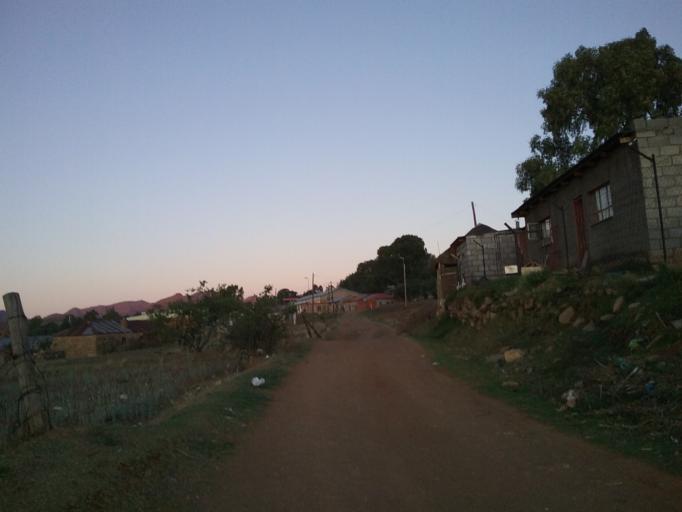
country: LS
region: Quthing
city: Quthing
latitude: -30.4087
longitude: 27.6998
